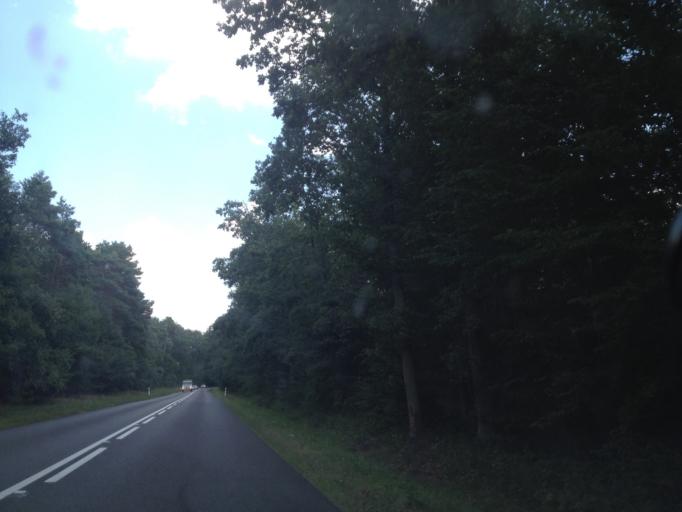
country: PL
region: Greater Poland Voivodeship
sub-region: Powiat poznanski
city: Kornik
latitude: 52.2468
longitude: 17.0425
